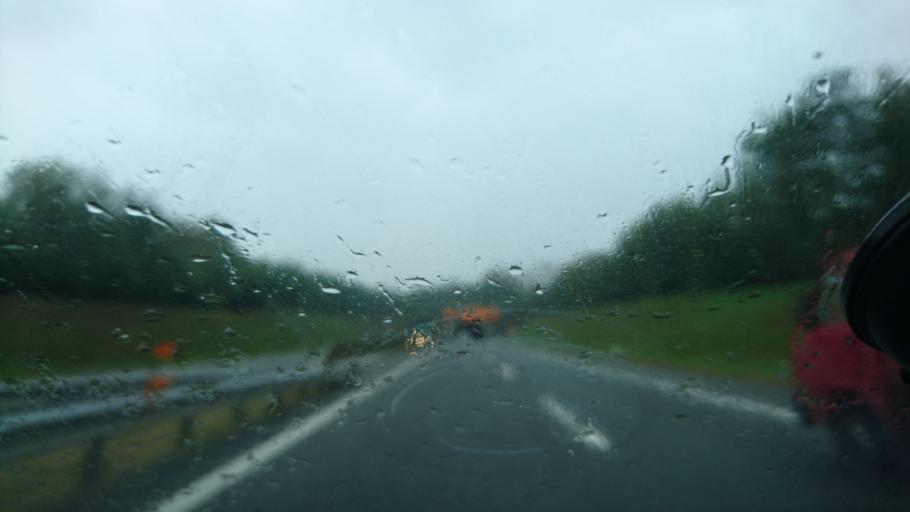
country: IT
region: Piedmont
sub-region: Provincia di Novara
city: Fontaneto D'Agogna
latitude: 45.6433
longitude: 8.4612
